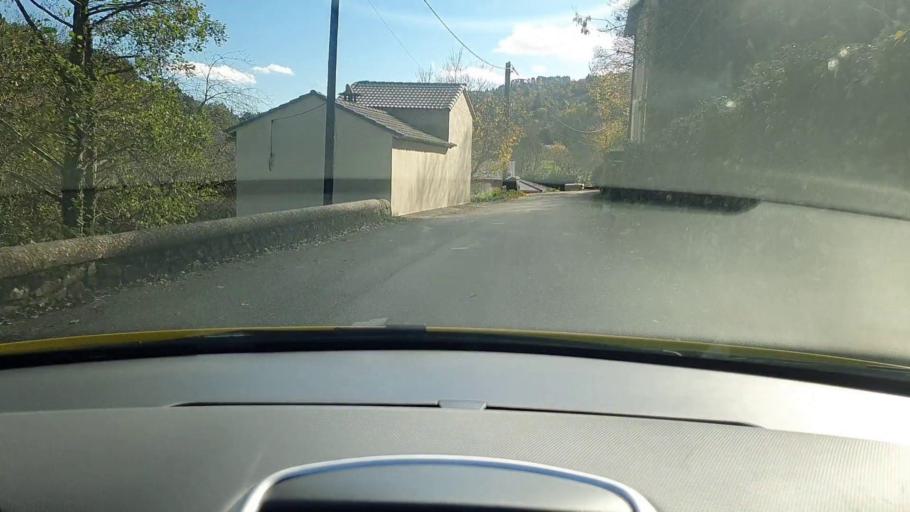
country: FR
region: Languedoc-Roussillon
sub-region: Departement du Gard
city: Valleraugue
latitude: 44.1615
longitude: 3.6738
